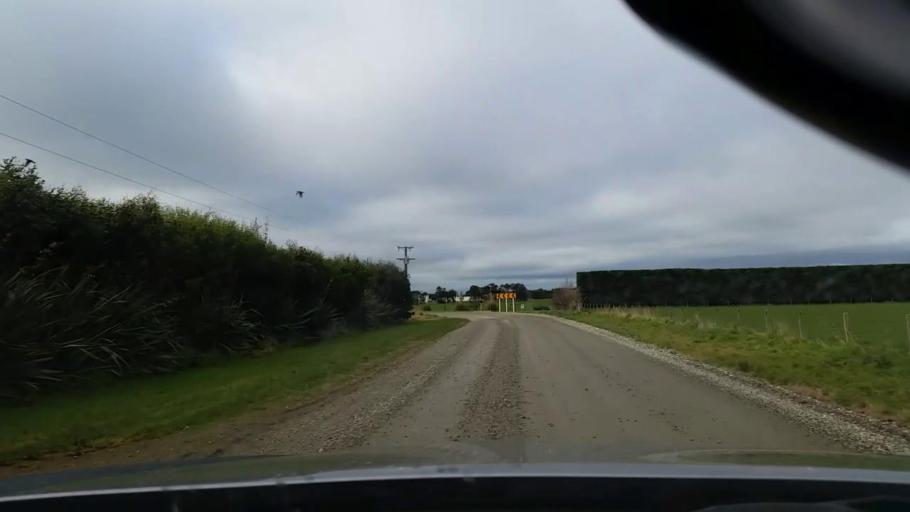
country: NZ
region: Southland
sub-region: Invercargill City
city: Invercargill
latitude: -46.3572
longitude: 168.4304
